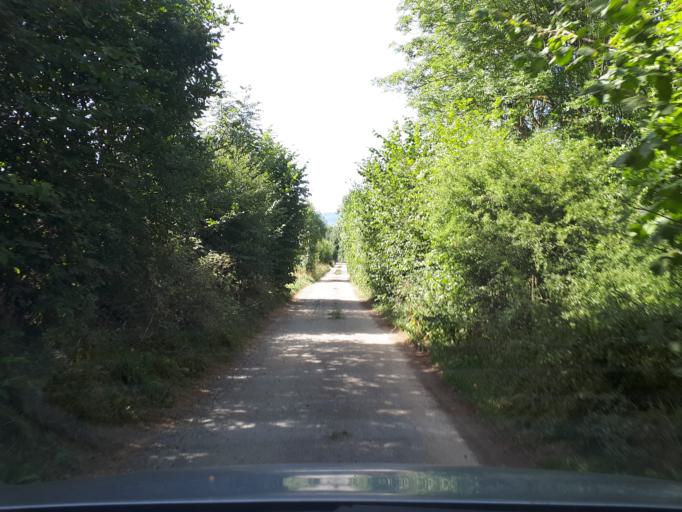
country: FR
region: Rhone-Alpes
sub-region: Departement de l'Isere
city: Pierre-Chatel
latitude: 44.9870
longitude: 5.7837
